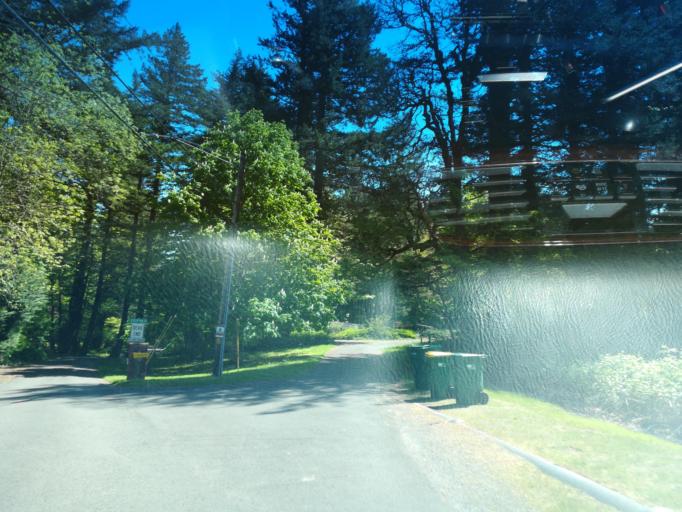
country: US
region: Oregon
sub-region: Multnomah County
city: Troutdale
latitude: 45.5345
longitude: -122.3782
